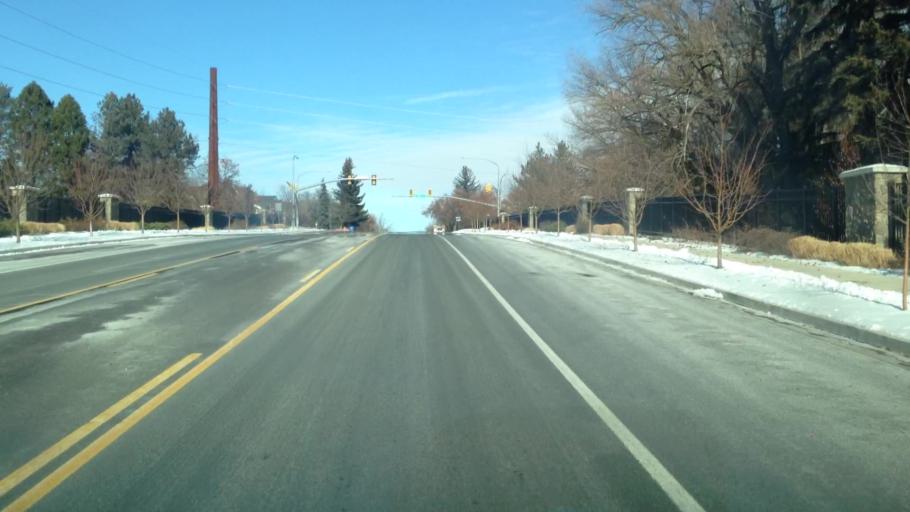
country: US
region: Utah
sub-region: Cache County
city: Logan
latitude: 41.7301
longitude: -111.8298
